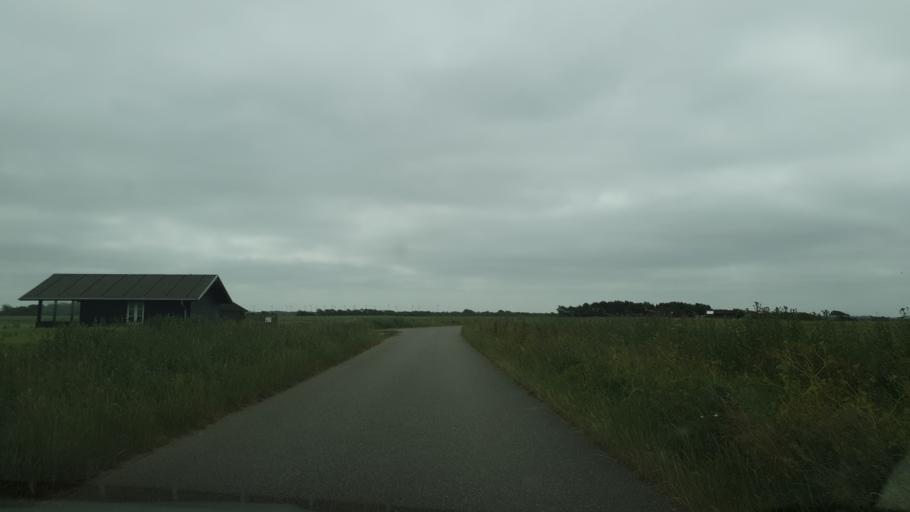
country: DK
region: Central Jutland
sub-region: Ringkobing-Skjern Kommune
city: Skjern
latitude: 55.9257
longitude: 8.4028
